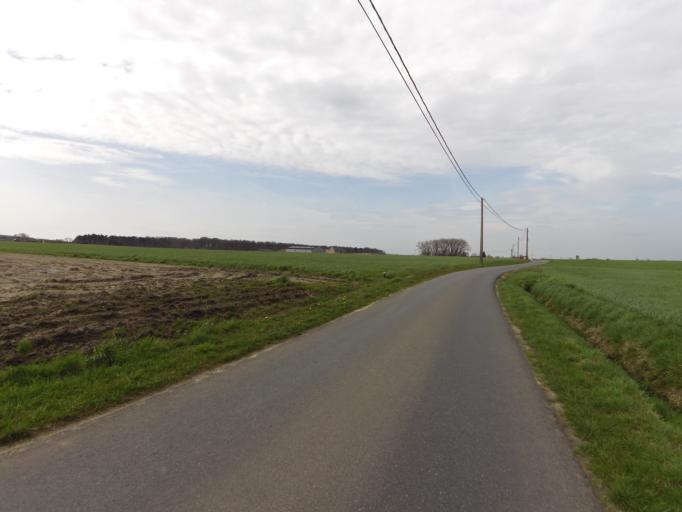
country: BE
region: Flanders
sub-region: Provincie West-Vlaanderen
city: Koekelare
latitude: 51.0674
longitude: 2.9799
